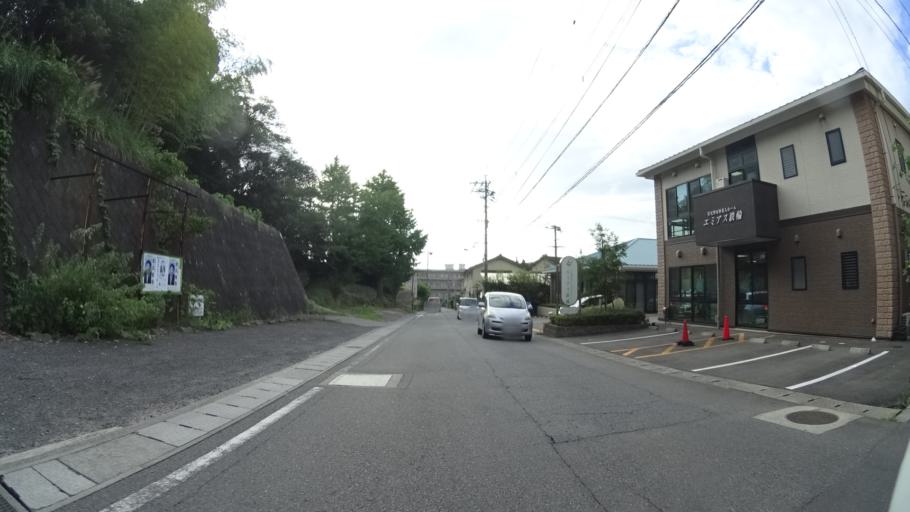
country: JP
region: Oita
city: Beppu
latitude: 33.3171
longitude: 131.4745
